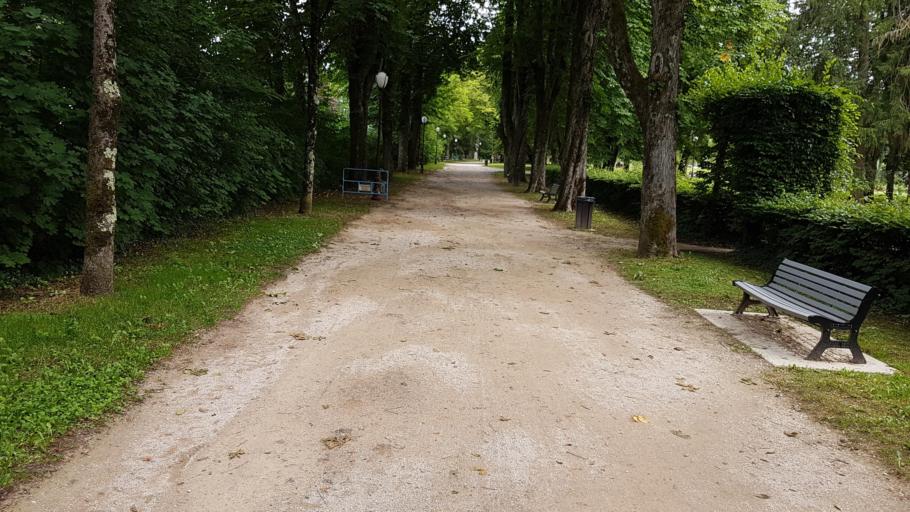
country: FR
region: Franche-Comte
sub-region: Departement du Jura
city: Lons-le-Saunier
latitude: 46.6726
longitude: 5.5623
